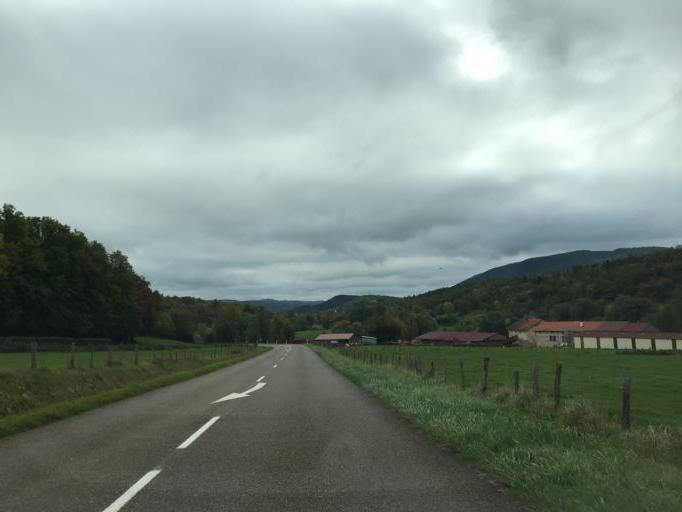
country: FR
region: Rhone-Alpes
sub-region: Departement de l'Ain
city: Cuisiat
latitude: 46.3541
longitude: 5.4364
